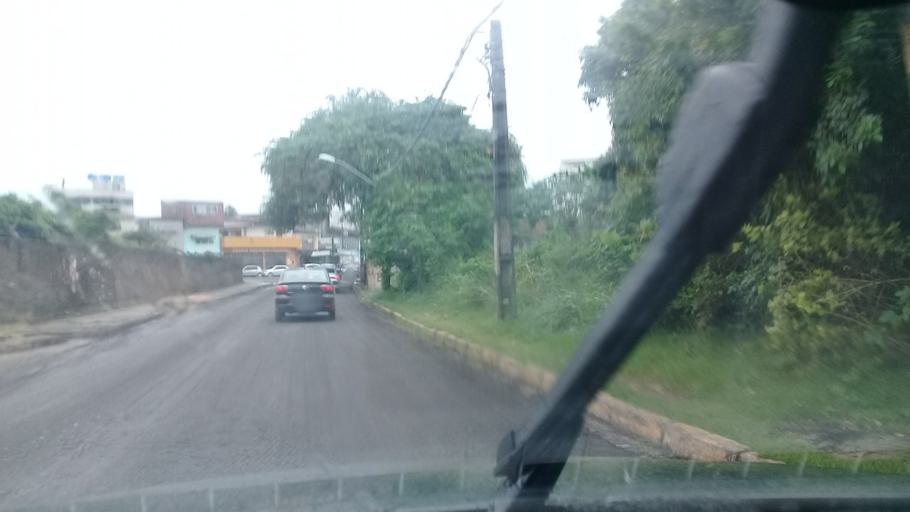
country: BR
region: Pernambuco
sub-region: Jaboatao Dos Guararapes
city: Jaboatao dos Guararapes
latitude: -8.0803
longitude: -34.9808
